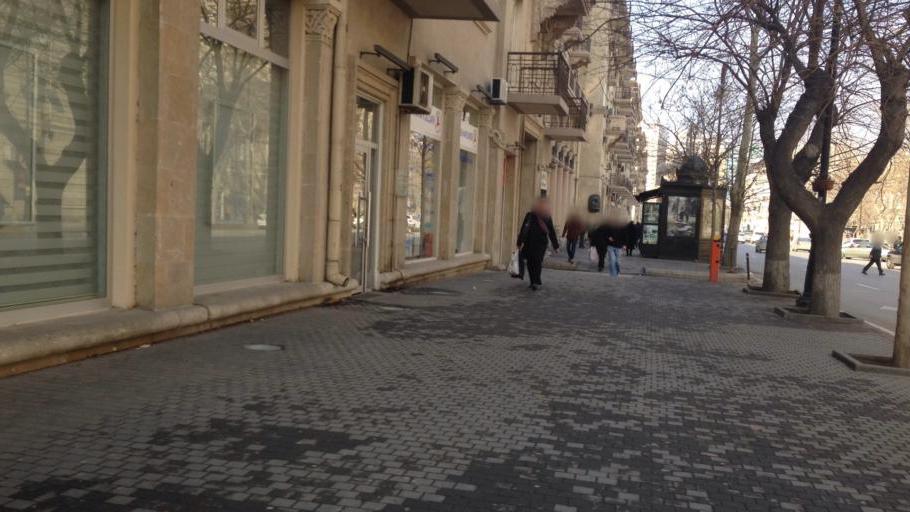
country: AZ
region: Baki
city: Badamdar
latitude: 40.3720
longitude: 49.8336
